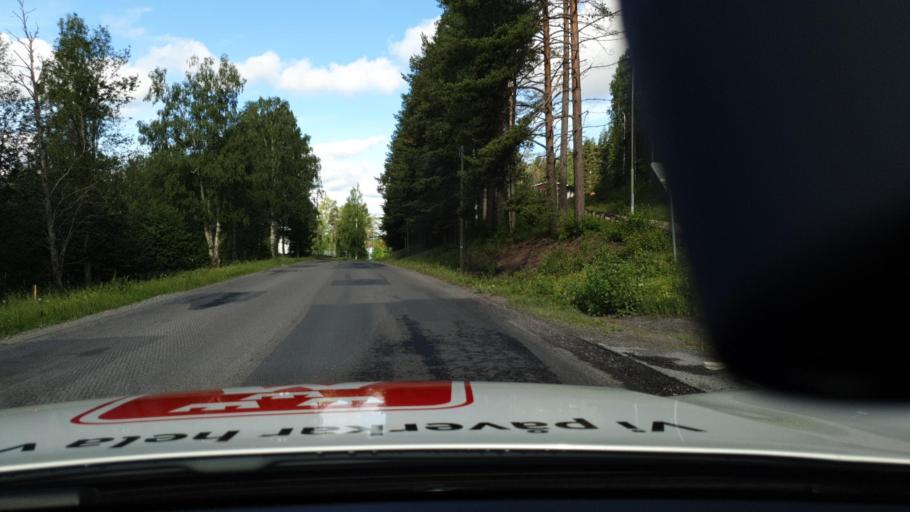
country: SE
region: Norrbotten
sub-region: Bodens Kommun
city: Boden
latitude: 65.8323
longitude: 21.6203
